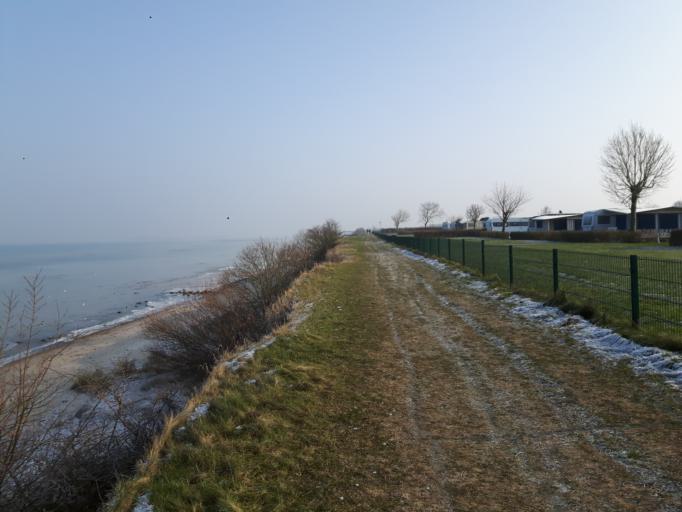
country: DE
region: Schleswig-Holstein
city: Stein
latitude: 54.4167
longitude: 10.2496
